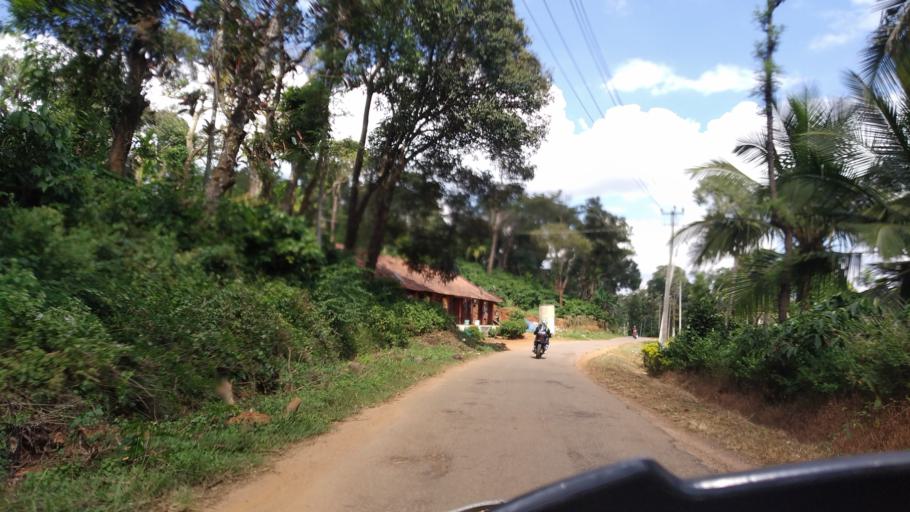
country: IN
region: Karnataka
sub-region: Kodagu
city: Ponnampet
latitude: 12.0270
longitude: 75.8940
